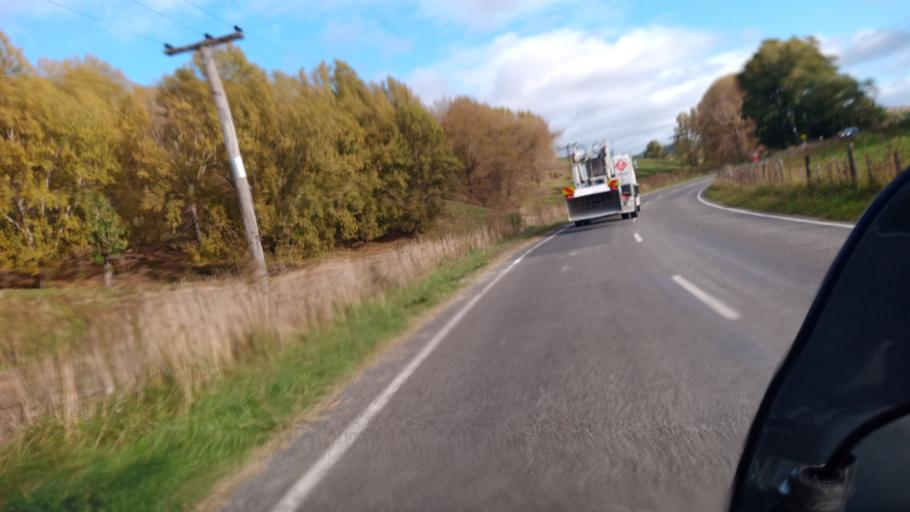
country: NZ
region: Gisborne
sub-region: Gisborne District
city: Gisborne
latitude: -38.5942
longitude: 177.7977
